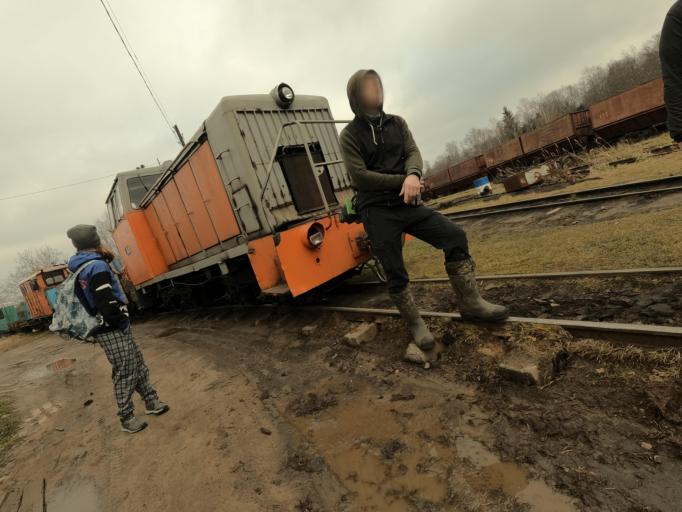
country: RU
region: Leningrad
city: Nurma
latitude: 59.6009
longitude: 31.2006
